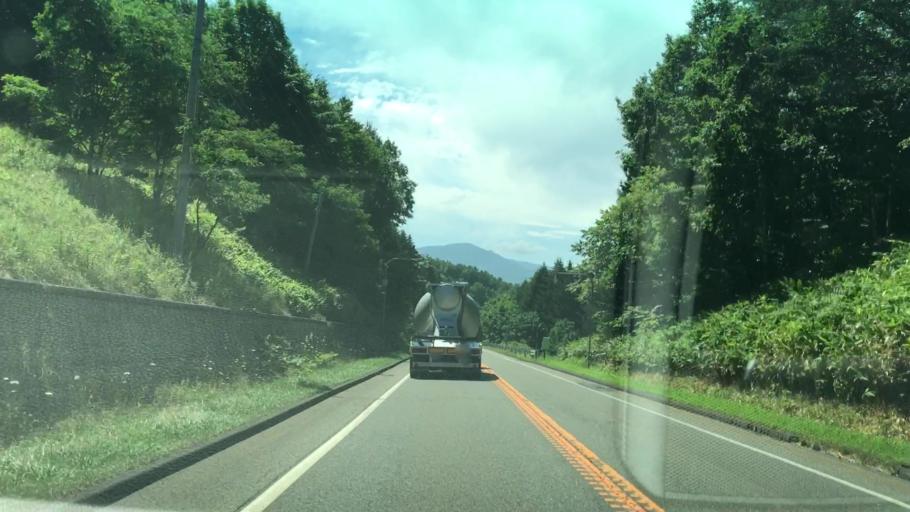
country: JP
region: Hokkaido
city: Shimo-furano
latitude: 42.8978
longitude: 142.4358
